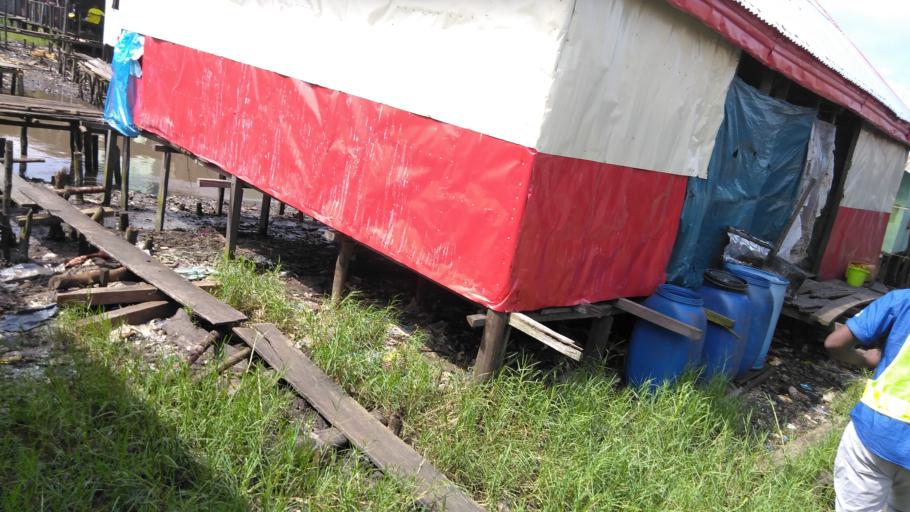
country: NG
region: Ondo
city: Igbekebo
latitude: 5.9246
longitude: 4.9635
